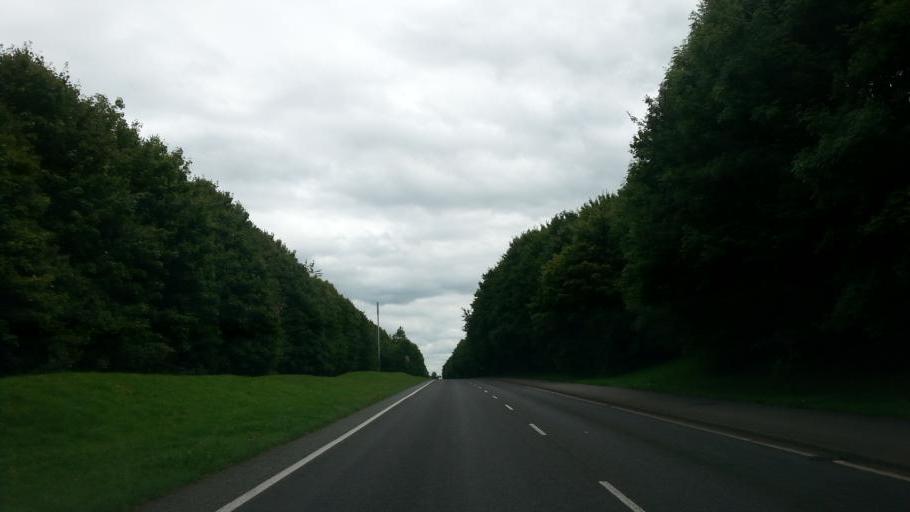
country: GB
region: England
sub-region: Northamptonshire
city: Northampton
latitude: 52.2734
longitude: -0.8232
